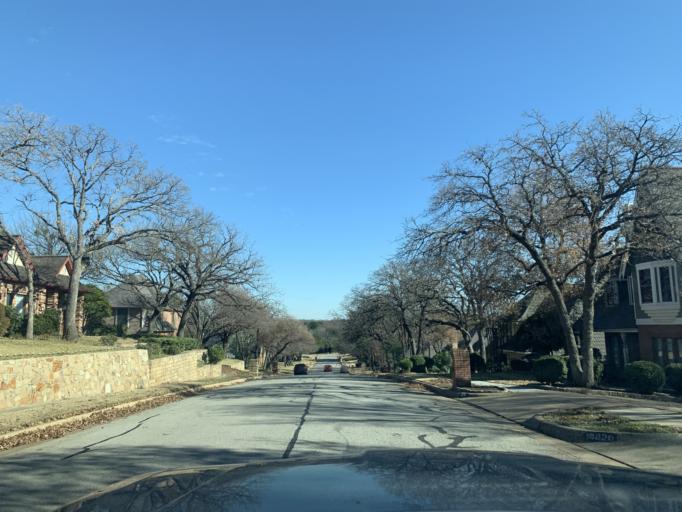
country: US
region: Texas
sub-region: Tarrant County
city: Bedford
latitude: 32.8485
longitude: -97.1578
